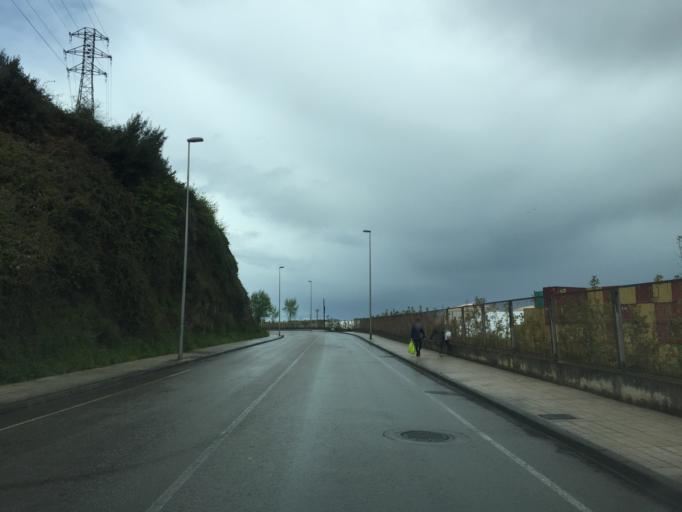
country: ES
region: Asturias
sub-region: Province of Asturias
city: Natahoyo
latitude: 43.5493
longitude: -5.6991
